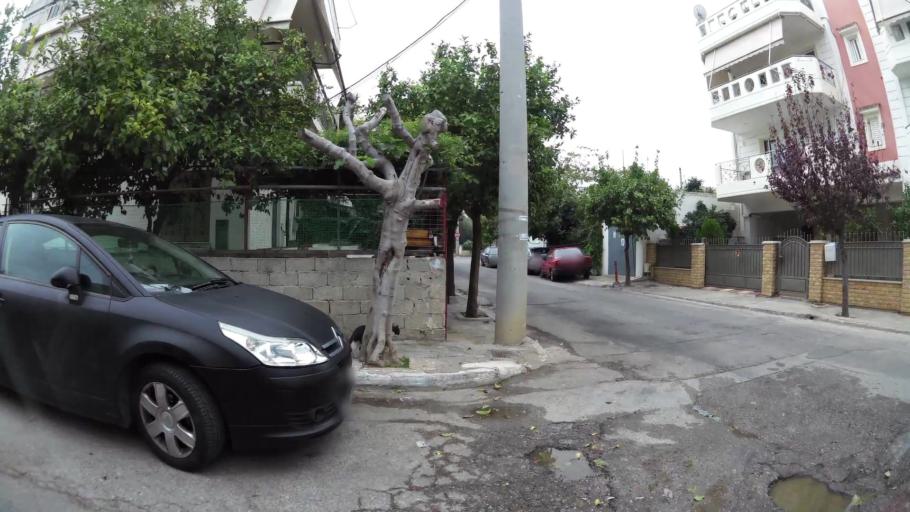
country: GR
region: Attica
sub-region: Nomarchia Athinas
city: Agioi Anargyroi
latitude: 38.0123
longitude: 23.7152
